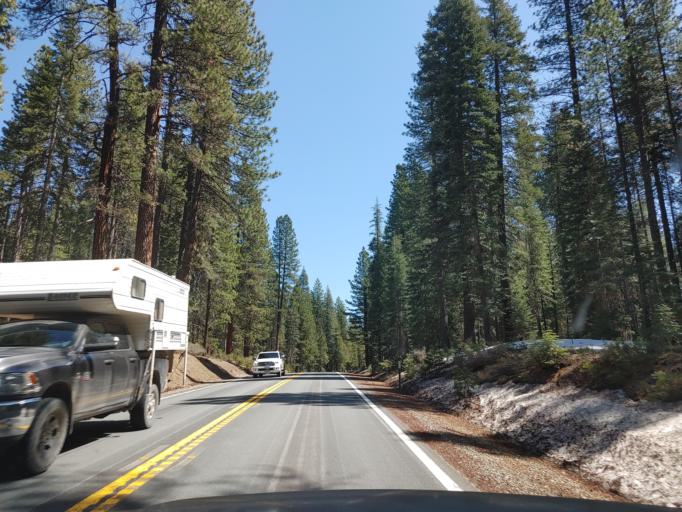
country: US
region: California
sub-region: Siskiyou County
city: McCloud
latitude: 41.2674
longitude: -121.9165
